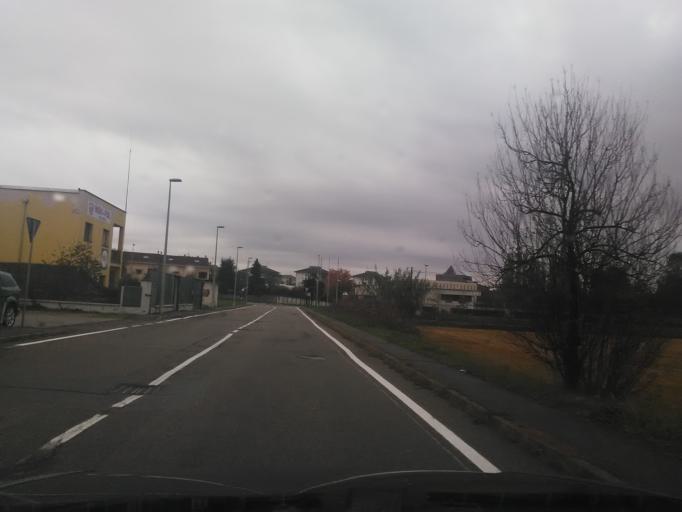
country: IT
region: Piedmont
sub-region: Provincia di Vercelli
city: Vercelli
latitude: 45.3186
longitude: 8.3986
